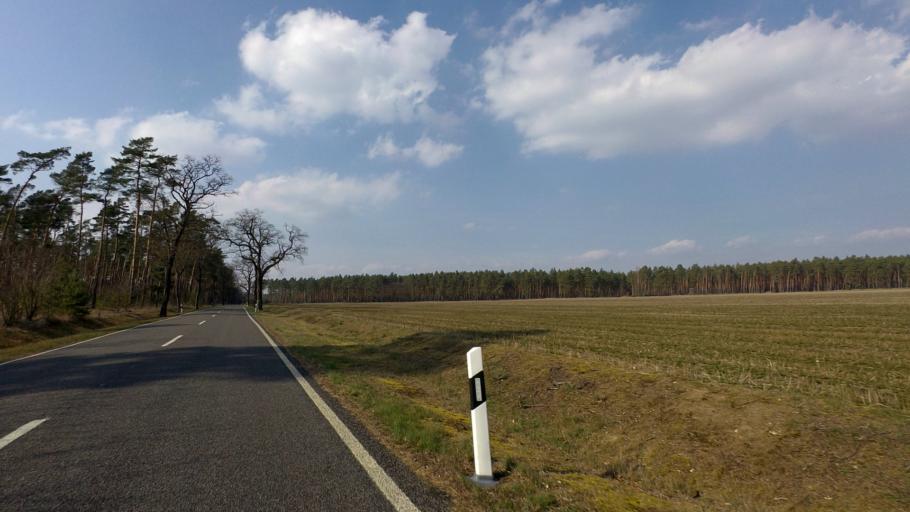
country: DE
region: Brandenburg
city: Dahme
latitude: 51.9227
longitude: 13.4724
